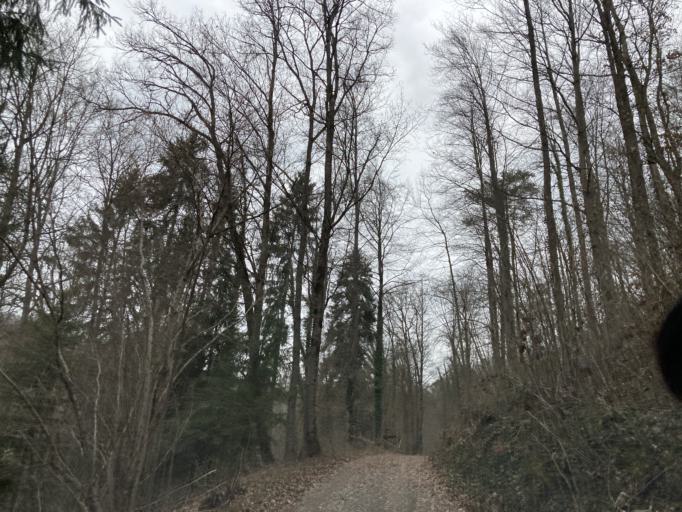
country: DE
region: Baden-Wuerttemberg
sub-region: Tuebingen Region
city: Hirrlingen
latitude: 48.4245
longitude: 8.8674
